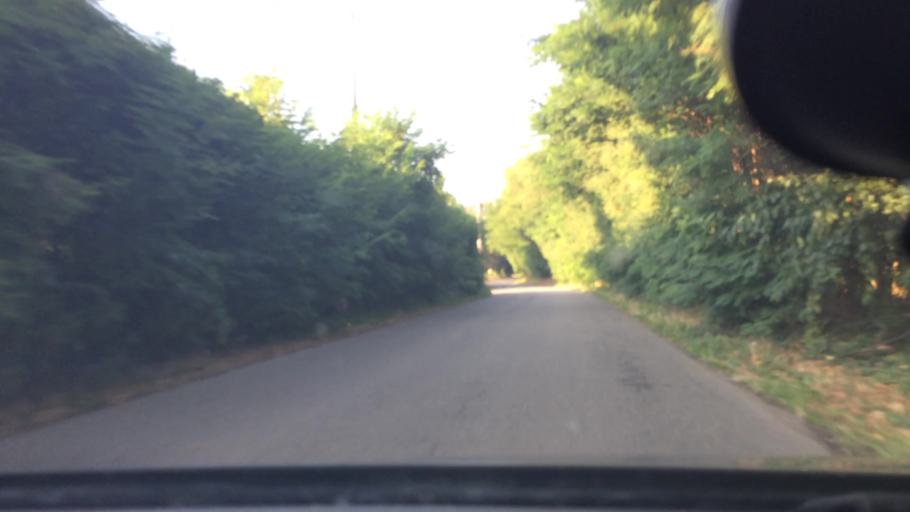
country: IT
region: Lombardy
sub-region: Citta metropolitana di Milano
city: Mantegazza
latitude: 45.5086
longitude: 8.9662
